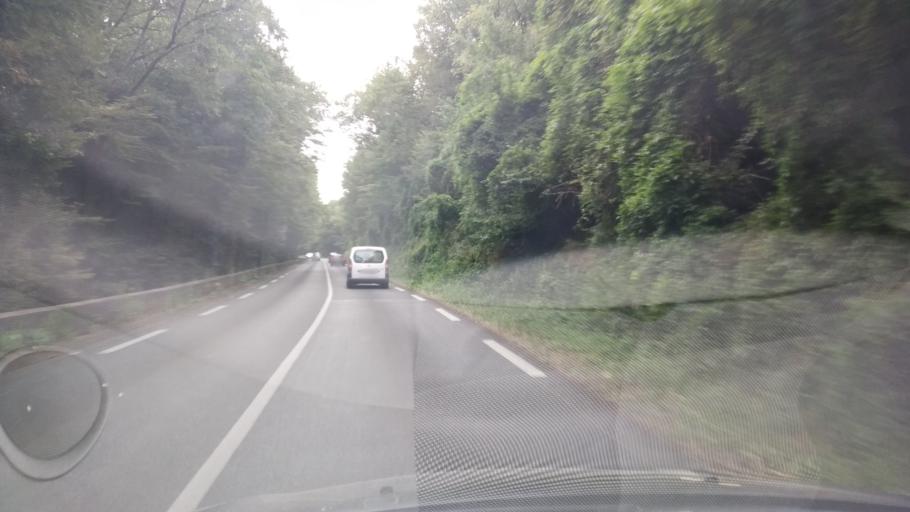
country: FR
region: Poitou-Charentes
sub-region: Departement de la Vienne
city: Saint-Benoit
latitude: 46.5484
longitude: 0.3510
